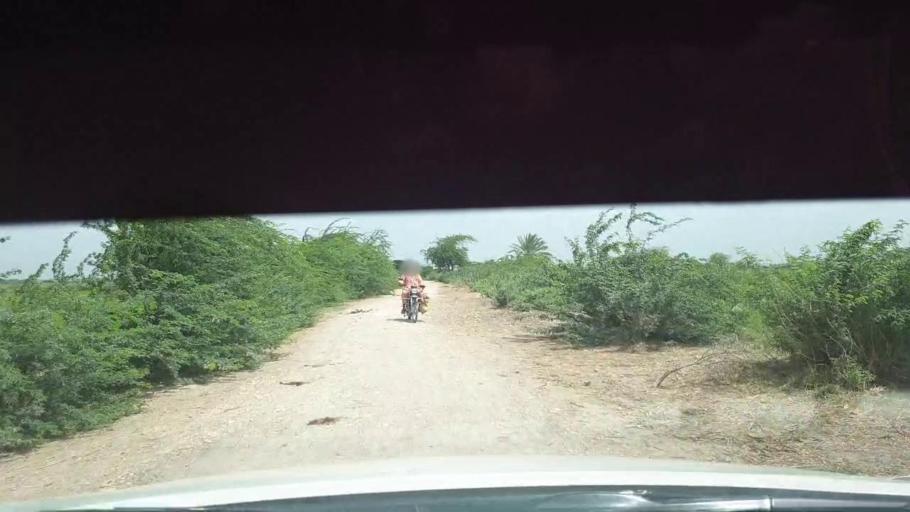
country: PK
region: Sindh
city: Kadhan
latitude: 24.4973
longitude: 68.9821
